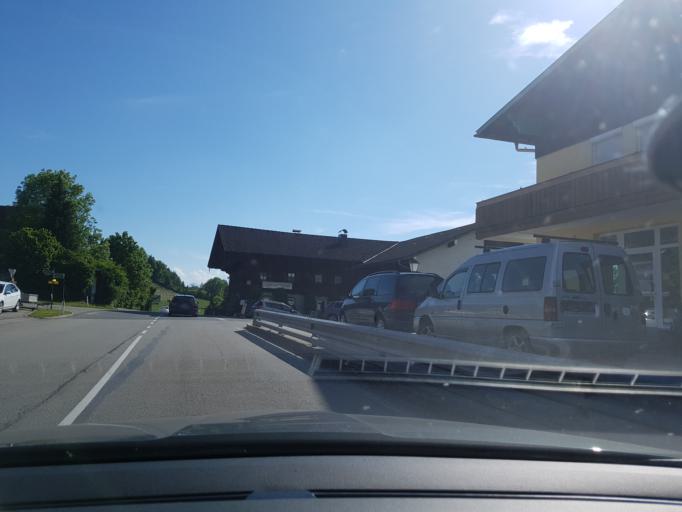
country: AT
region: Salzburg
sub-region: Politischer Bezirk Salzburg-Umgebung
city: Mattsee
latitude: 47.9657
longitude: 13.1000
